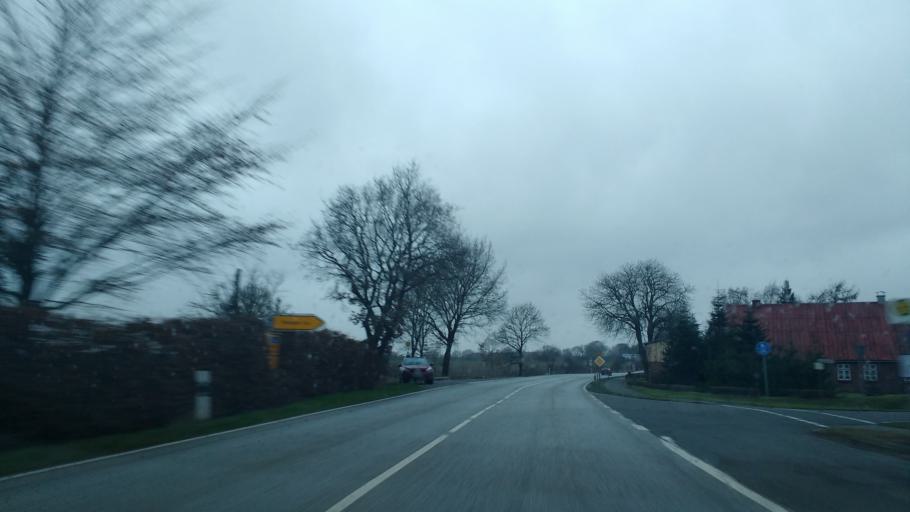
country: DE
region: Schleswig-Holstein
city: Peissen
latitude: 54.0224
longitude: 9.5926
